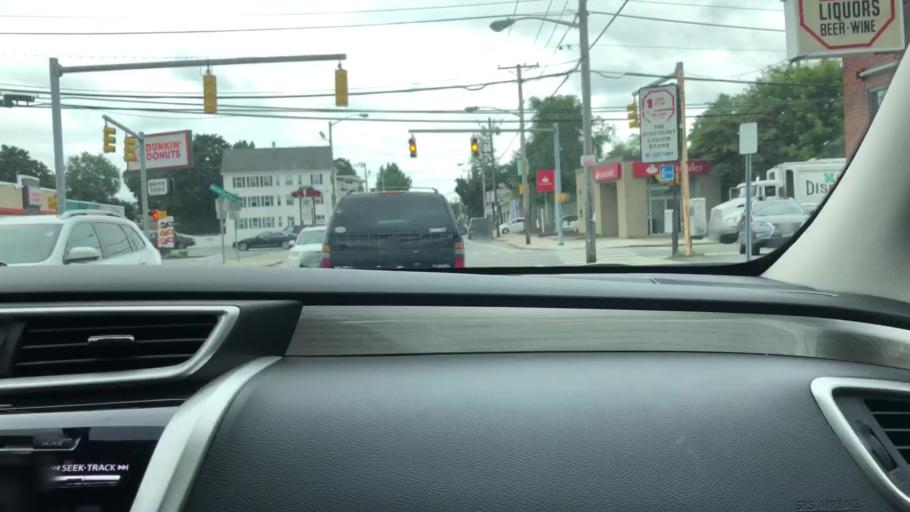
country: US
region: Rhode Island
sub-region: Providence County
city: Central Falls
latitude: 41.8715
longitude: -71.4139
